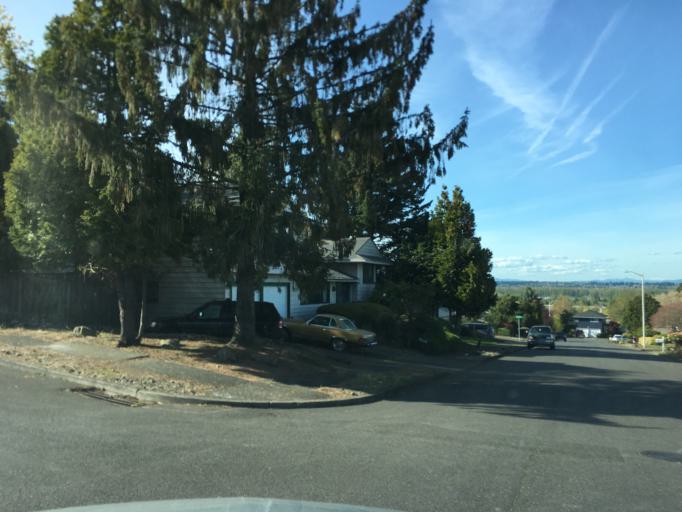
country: US
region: Oregon
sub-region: Multnomah County
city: Lents
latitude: 45.5452
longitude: -122.5189
